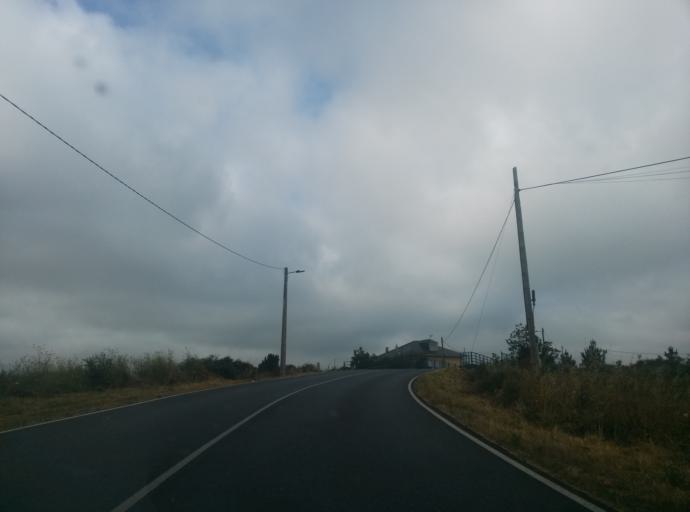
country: ES
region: Galicia
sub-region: Provincia de Lugo
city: Lugo
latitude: 43.0585
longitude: -7.5679
